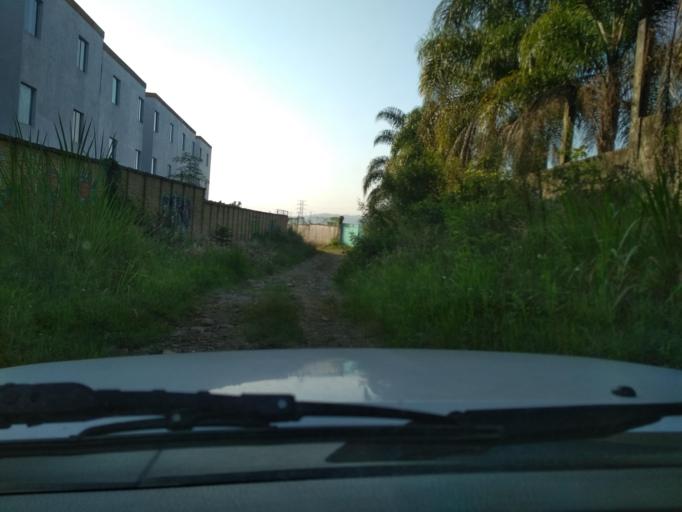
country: MX
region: Veracruz
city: Cordoba
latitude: 18.8680
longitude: -96.9326
